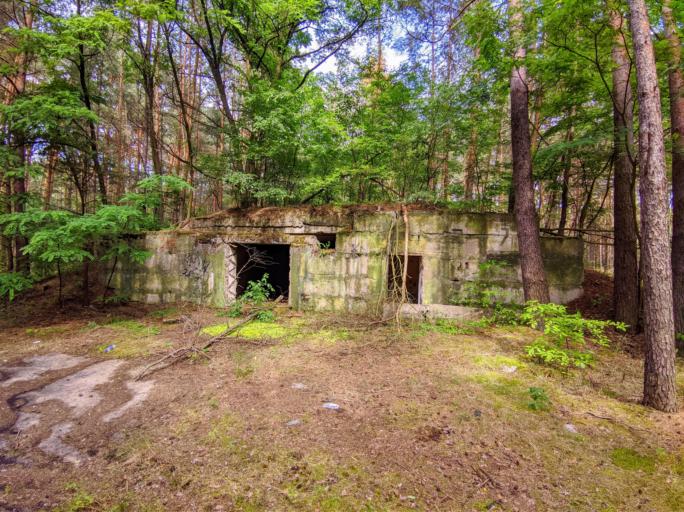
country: PL
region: Lubusz
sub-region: Powiat zaganski
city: Szprotawa
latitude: 51.5559
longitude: 15.6011
